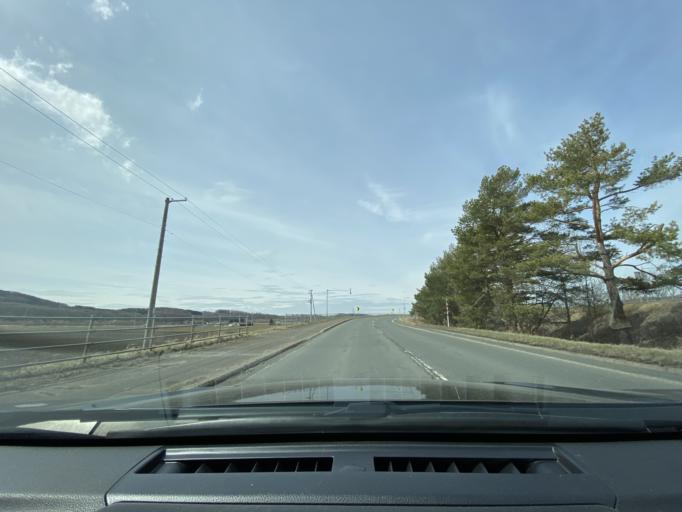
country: JP
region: Hokkaido
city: Kitami
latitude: 43.8011
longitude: 143.7852
